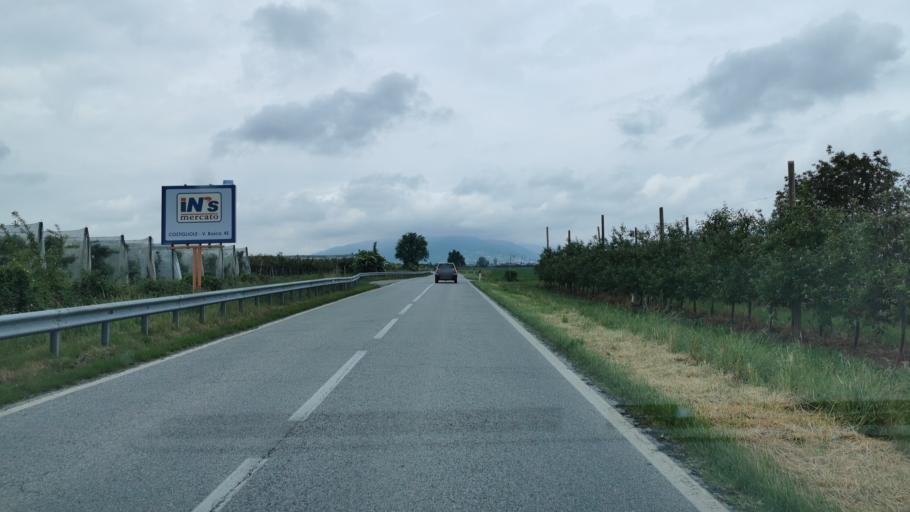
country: IT
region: Piedmont
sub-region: Provincia di Cuneo
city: Lagnasco
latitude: 44.5903
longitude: 7.5492
